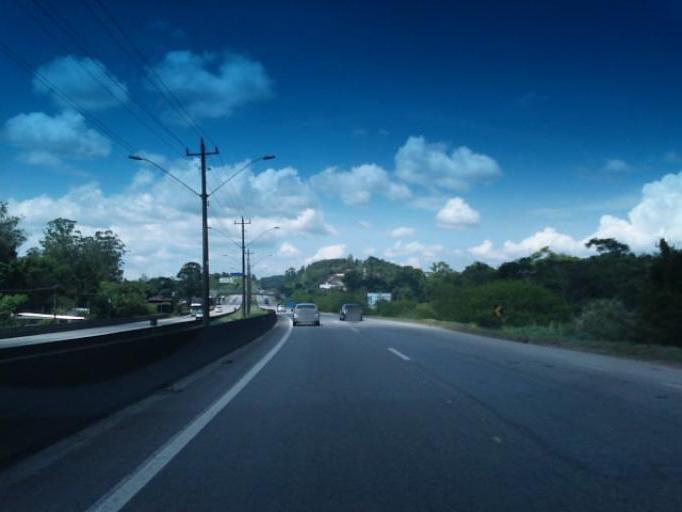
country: BR
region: Sao Paulo
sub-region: Sao Lourenco Da Serra
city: Sao Lourenco da Serra
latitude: -23.8921
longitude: -46.9836
